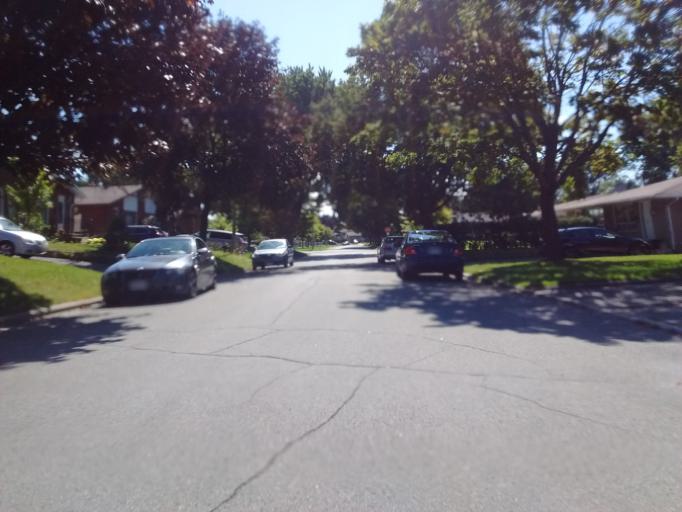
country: CA
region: Ontario
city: Ottawa
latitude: 45.4343
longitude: -75.6383
